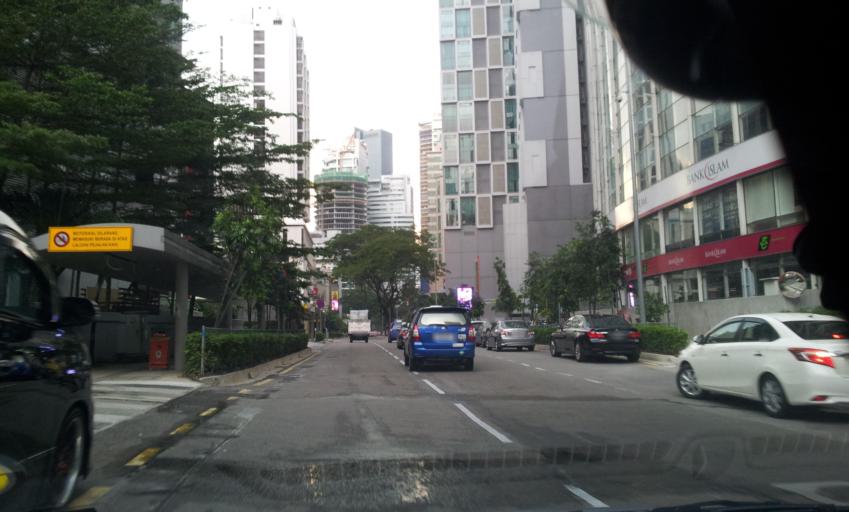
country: MY
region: Kuala Lumpur
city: Kuala Lumpur
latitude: 3.1526
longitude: 101.7114
